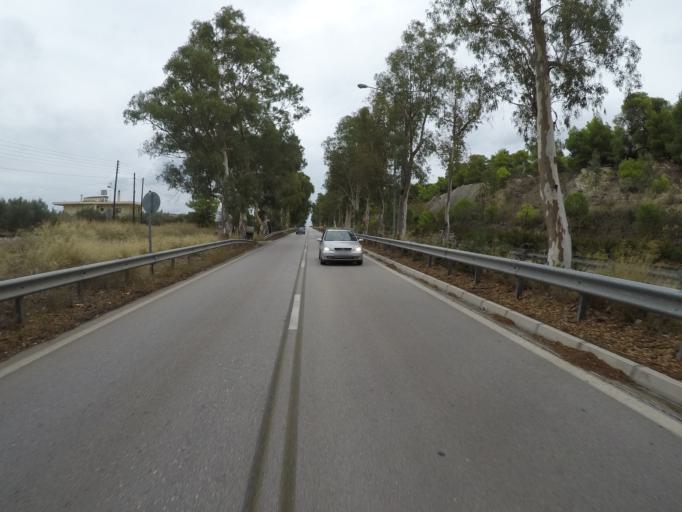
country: GR
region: Peloponnese
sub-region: Nomos Korinthias
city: Kyras Vrysi
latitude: 37.9356
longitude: 22.9869
